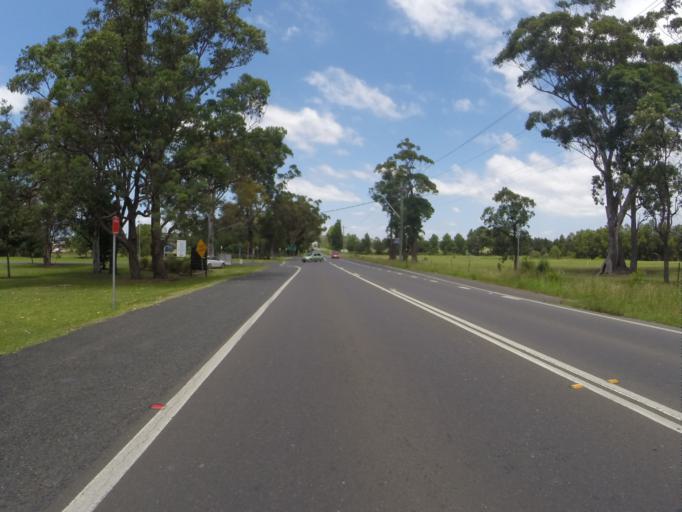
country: AU
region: New South Wales
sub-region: Shoalhaven Shire
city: Berry
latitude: -34.7752
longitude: 150.6849
